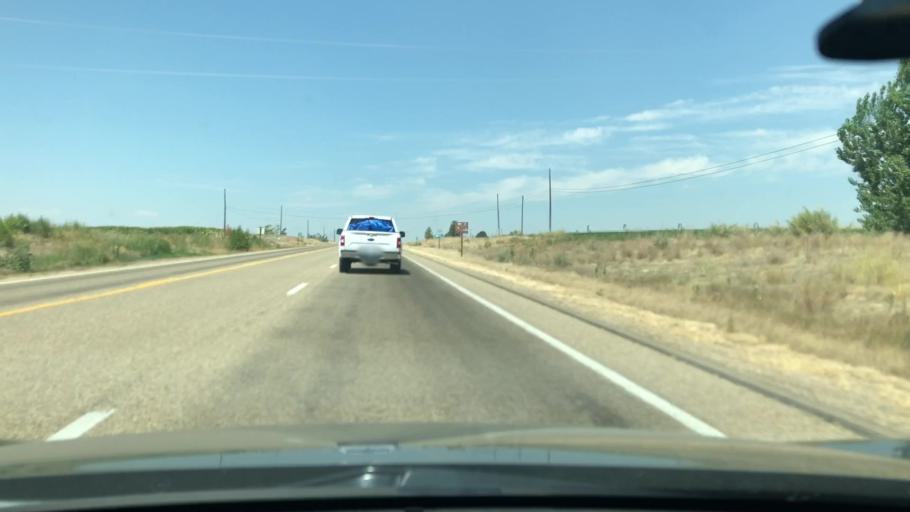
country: US
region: Idaho
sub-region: Canyon County
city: Parma
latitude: 43.8201
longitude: -116.9544
